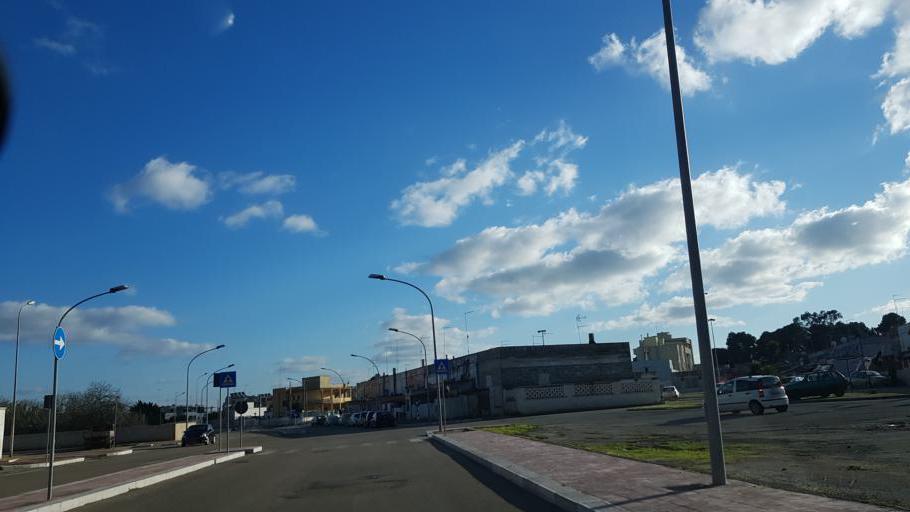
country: IT
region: Apulia
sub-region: Provincia di Brindisi
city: Brindisi
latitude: 40.6468
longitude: 17.9217
